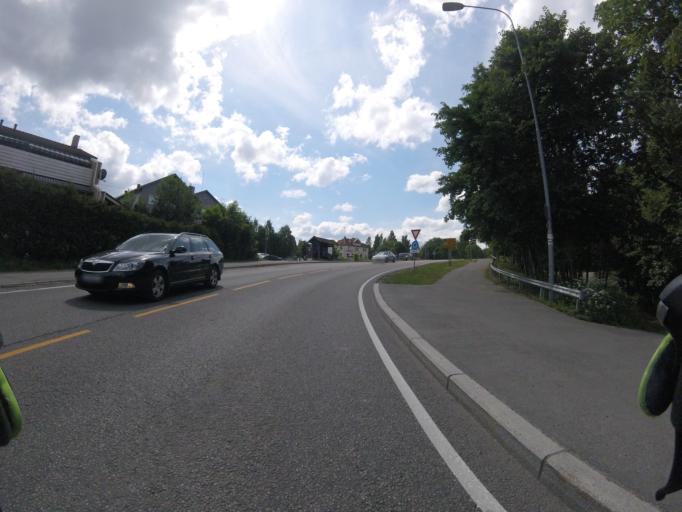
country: NO
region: Akershus
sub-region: Skedsmo
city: Lillestrom
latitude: 59.9581
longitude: 11.0165
